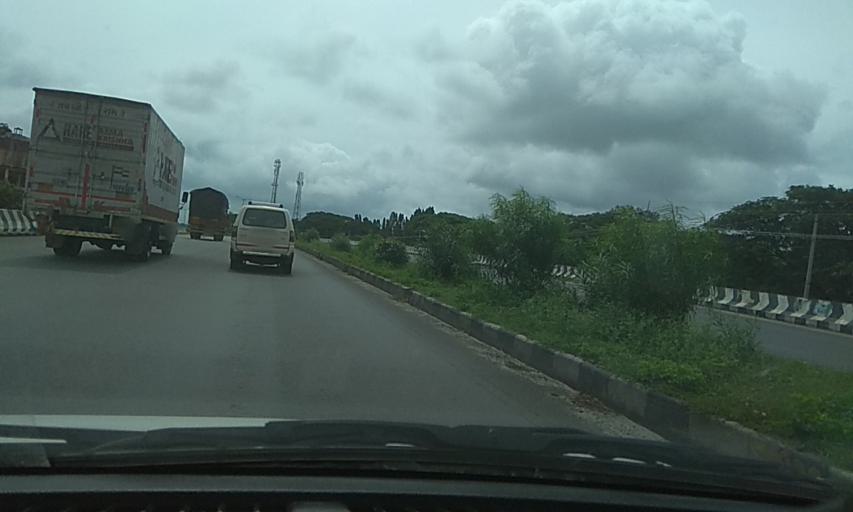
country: IN
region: Karnataka
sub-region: Davanagere
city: Mayakonda
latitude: 14.3784
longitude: 76.0952
